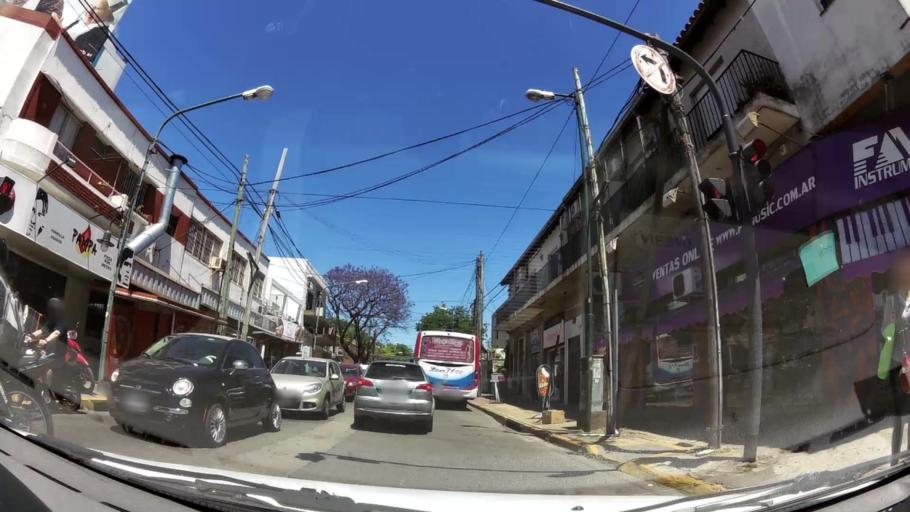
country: AR
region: Buenos Aires
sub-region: Partido de Vicente Lopez
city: Olivos
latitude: -34.4978
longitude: -58.4979
